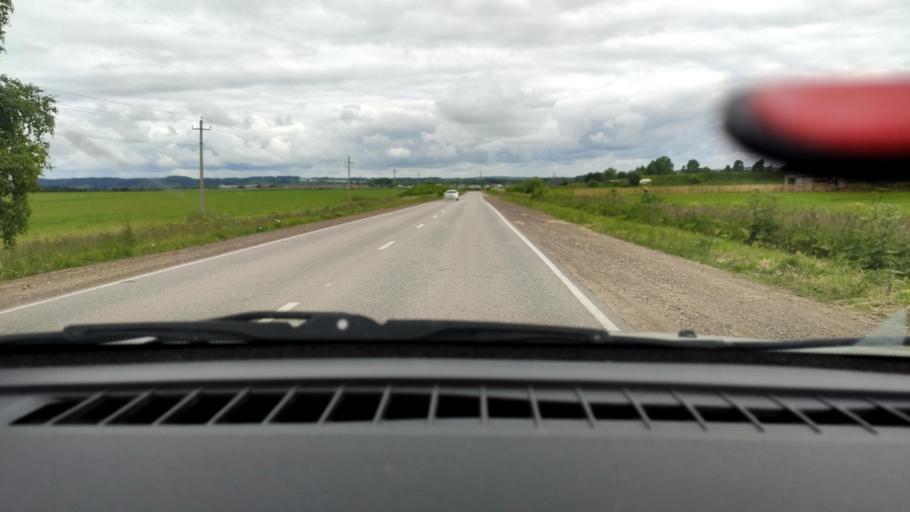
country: RU
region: Perm
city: Ust'-Kachka
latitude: 58.0702
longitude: 55.6261
